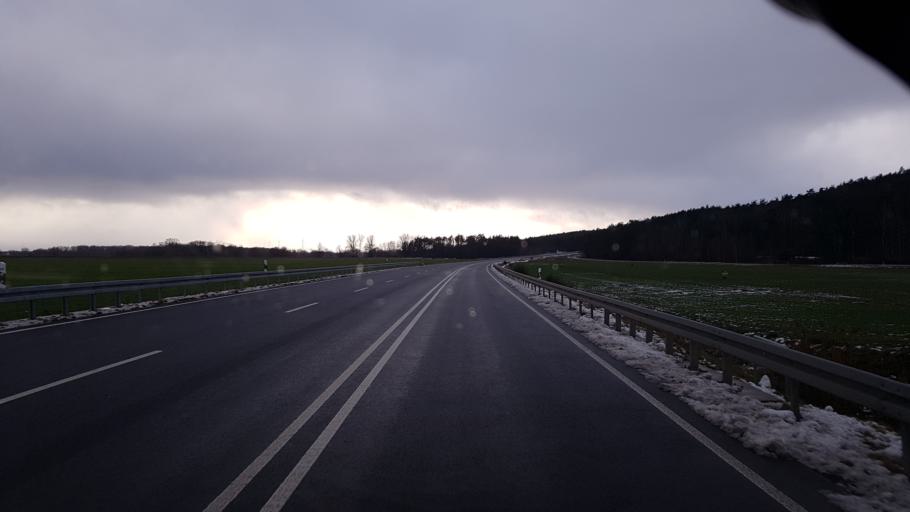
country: DE
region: Brandenburg
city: Schenkendobern
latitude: 51.8627
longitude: 14.6143
